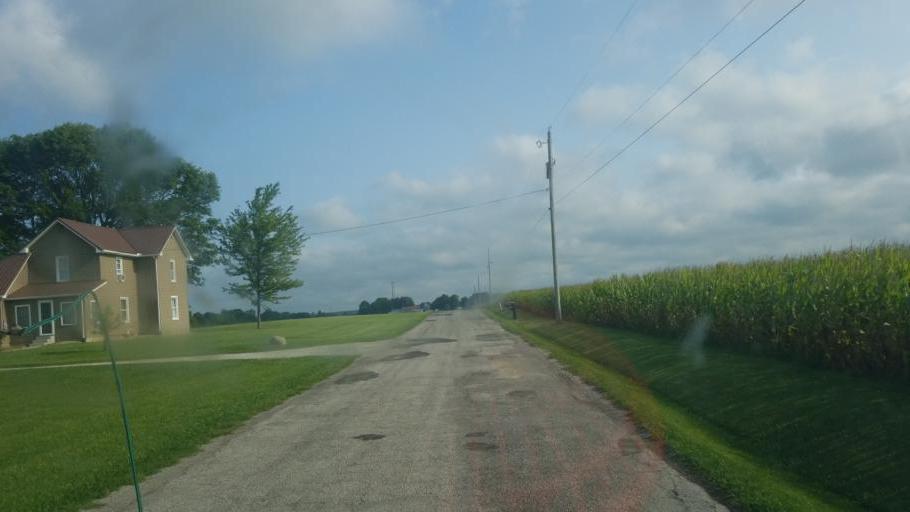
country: US
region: Ohio
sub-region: Delaware County
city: Ashley
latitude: 40.4656
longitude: -83.0082
